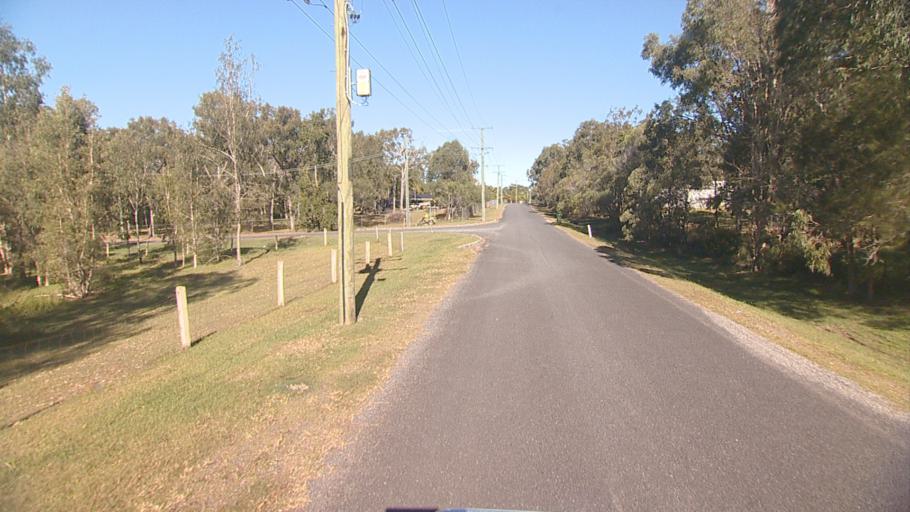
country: AU
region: Queensland
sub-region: Logan
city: Park Ridge South
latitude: -27.7128
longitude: 153.0411
